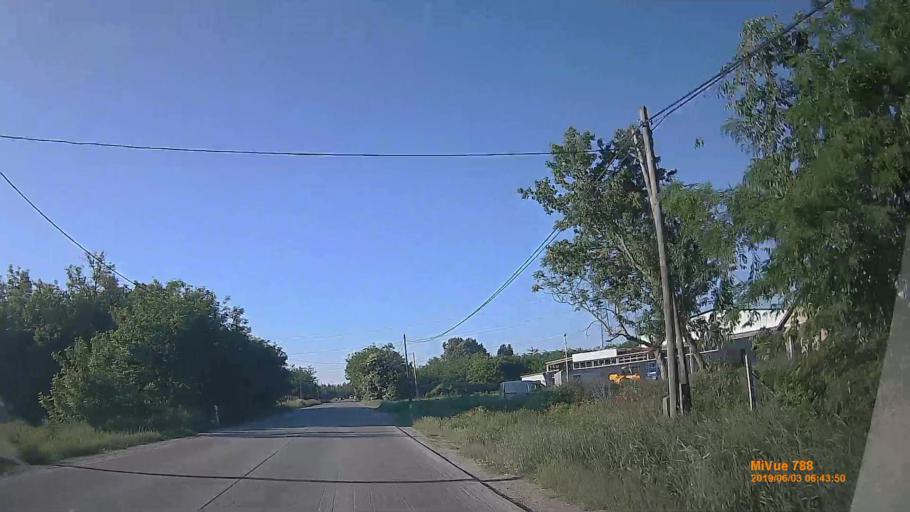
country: HU
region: Pest
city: Bugyi
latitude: 47.2506
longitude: 19.1275
